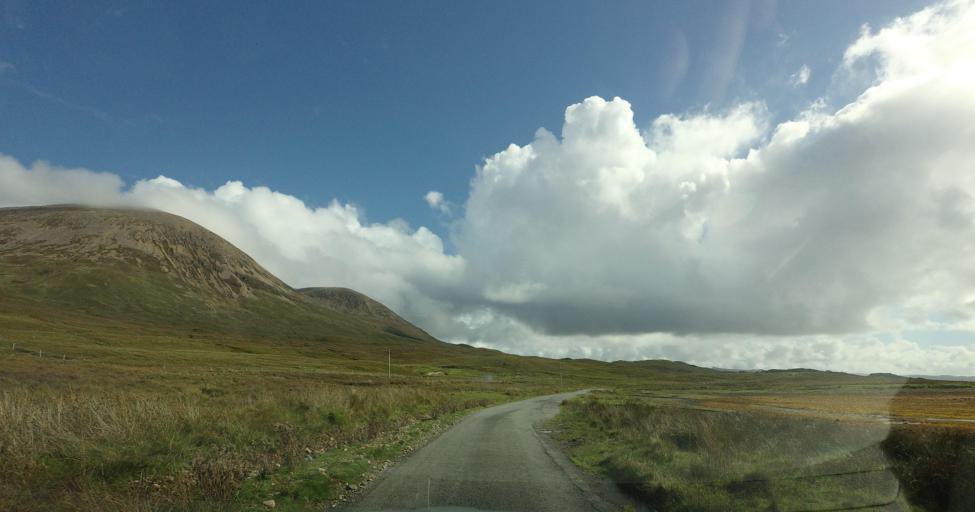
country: GB
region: Scotland
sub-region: Highland
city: Portree
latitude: 57.2254
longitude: -6.0319
